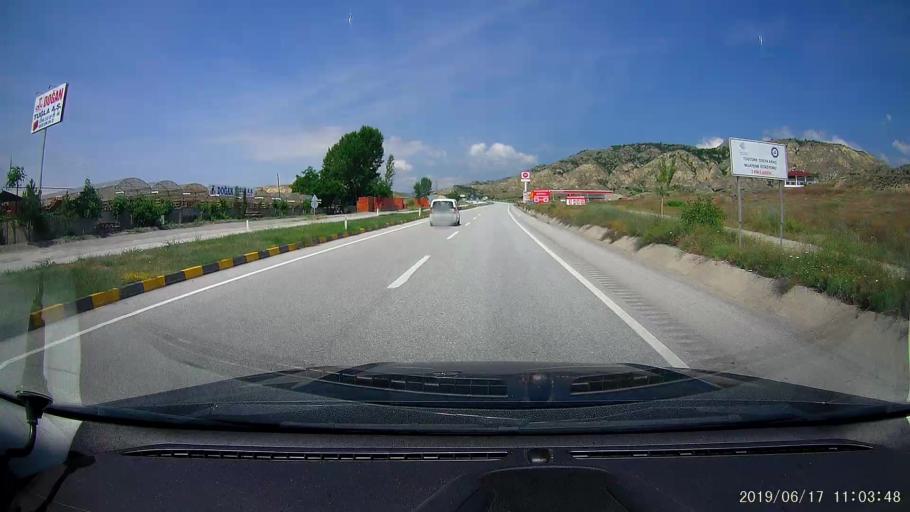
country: TR
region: Kastamonu
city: Tosya
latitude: 41.0194
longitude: 34.1089
